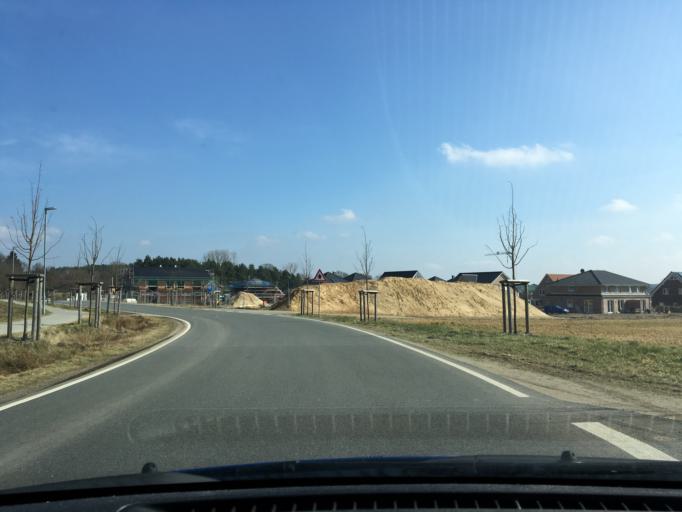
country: DE
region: Lower Saxony
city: Salzhausen
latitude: 53.2240
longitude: 10.1590
